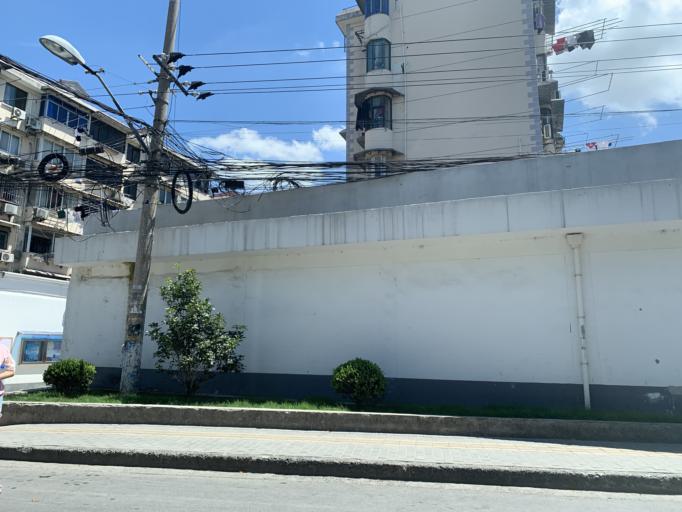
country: CN
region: Shanghai Shi
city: Huamu
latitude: 31.1743
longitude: 121.5358
